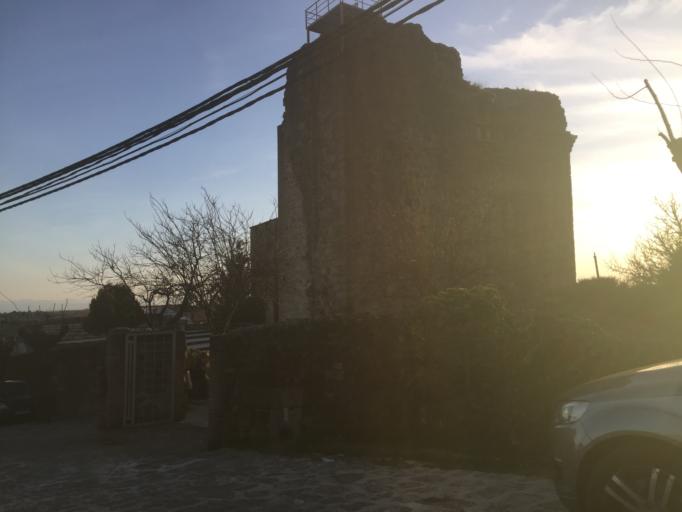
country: ES
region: Extremadura
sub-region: Provincia de Caceres
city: Valverde de la Vera
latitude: 40.1239
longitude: -5.4950
